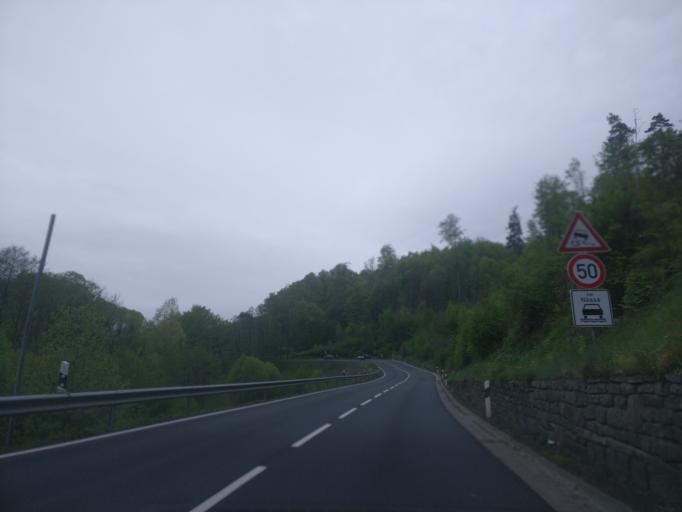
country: DE
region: Lower Saxony
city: Buhren
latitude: 51.4468
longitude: 9.6890
